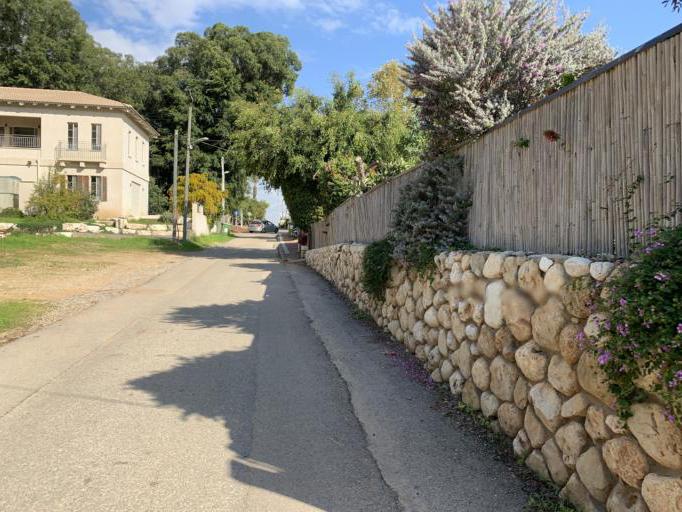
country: IL
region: Central District
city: Ra'anana
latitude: 32.1668
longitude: 34.8755
